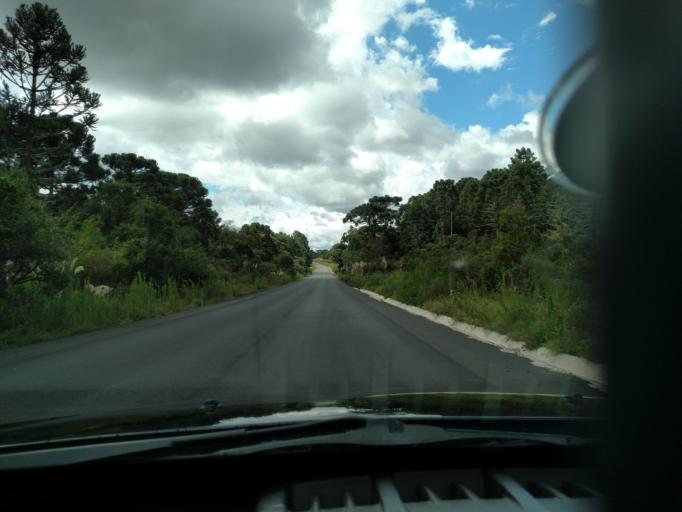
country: BR
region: Santa Catarina
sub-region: Lages
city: Lages
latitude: -27.9551
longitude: -50.0961
